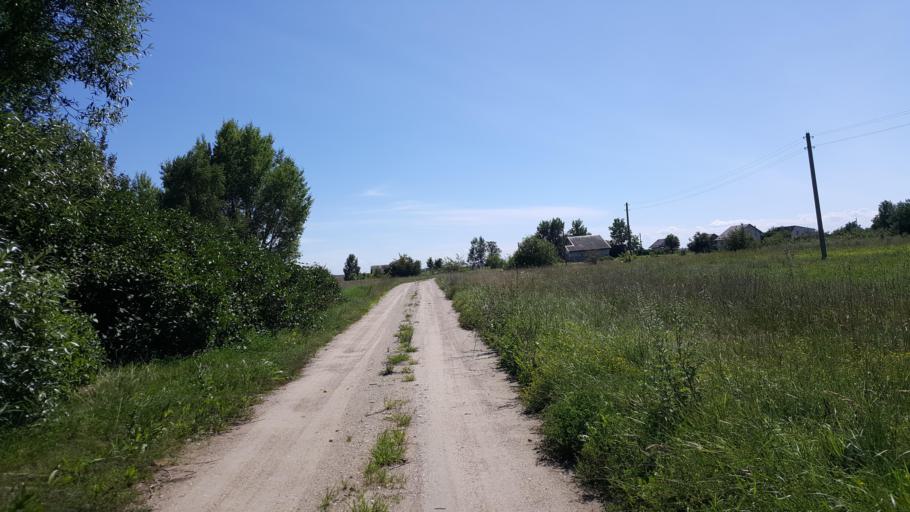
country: BY
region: Brest
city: Charnawchytsy
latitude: 52.2122
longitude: 23.7987
